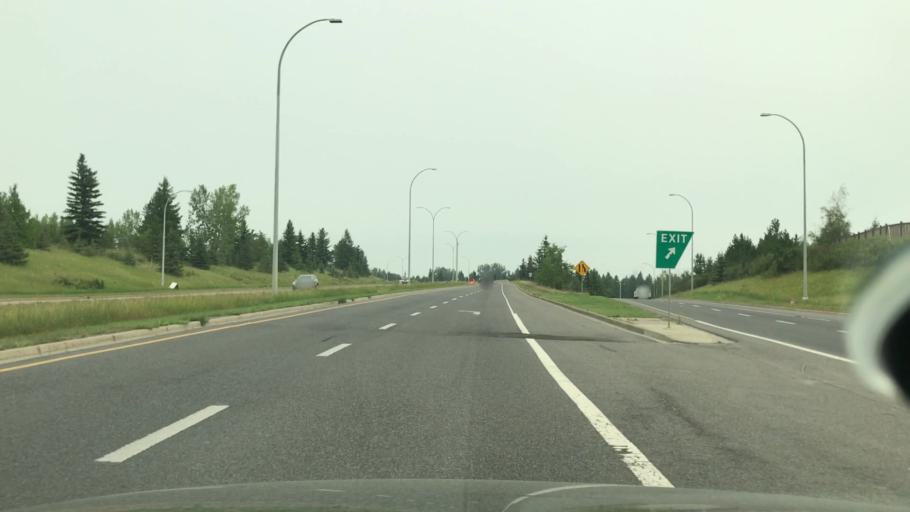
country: CA
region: Alberta
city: Edmonton
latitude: 53.4798
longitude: -113.5721
